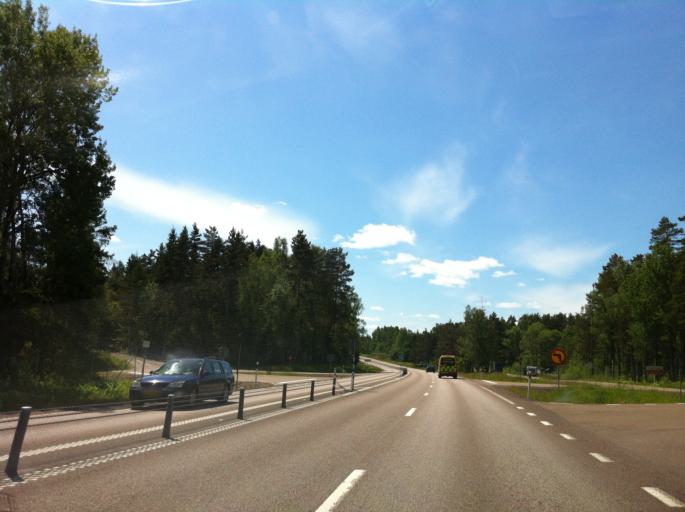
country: SE
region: Vaestra Goetaland
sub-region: Melleruds Kommun
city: Mellerud
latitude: 58.8259
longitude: 12.5263
